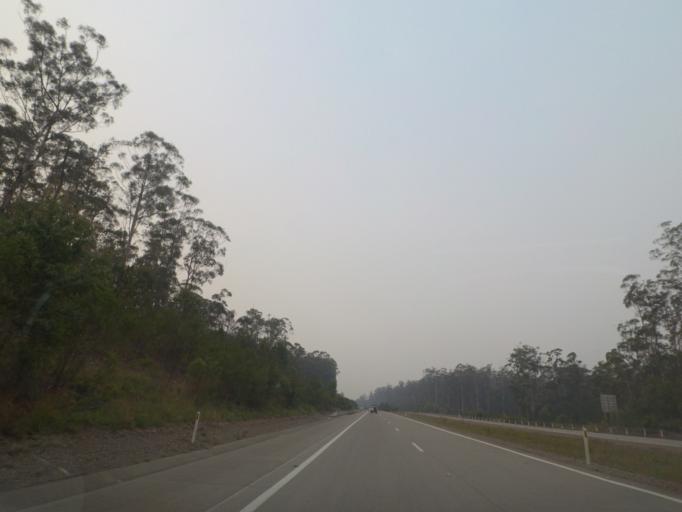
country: AU
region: New South Wales
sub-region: Kempsey
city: Frederickton
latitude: -30.8916
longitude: 152.9315
